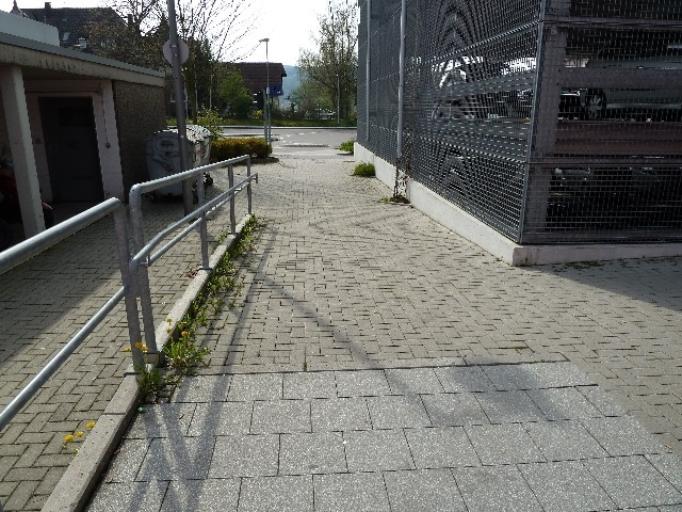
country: DE
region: Baden-Wuerttemberg
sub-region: Karlsruhe Region
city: Obrigheim
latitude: 49.3496
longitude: 9.1119
